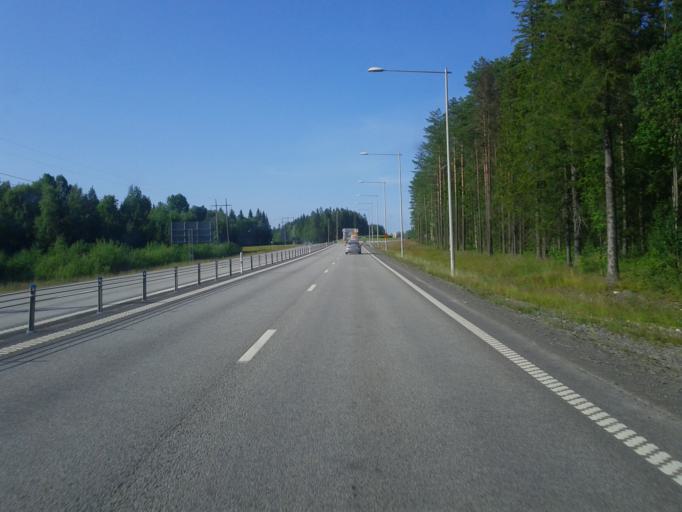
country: SE
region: Vaesterbotten
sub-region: Umea Kommun
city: Ersmark
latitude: 63.8157
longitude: 20.3269
